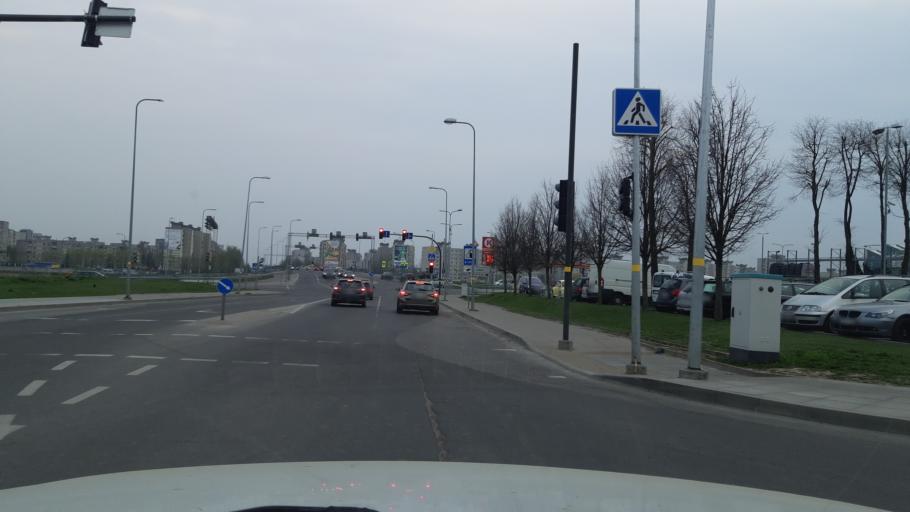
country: LT
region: Kauno apskritis
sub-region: Kaunas
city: Silainiai
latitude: 54.9395
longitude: 23.8997
